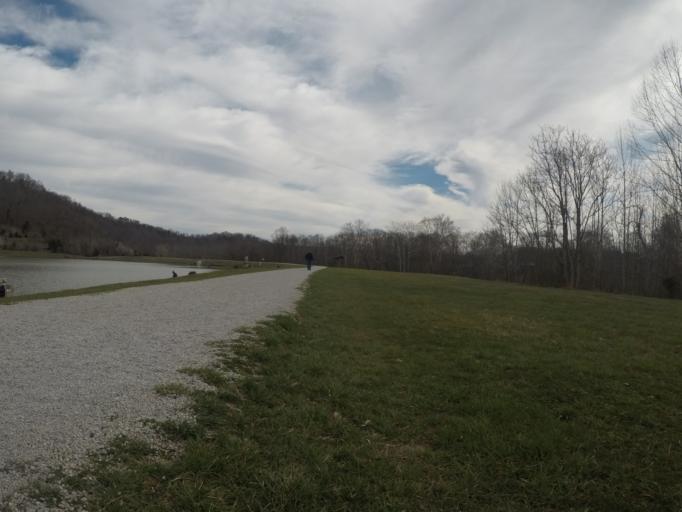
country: US
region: West Virginia
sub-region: Cabell County
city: Barboursville
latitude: 38.3860
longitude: -82.2997
